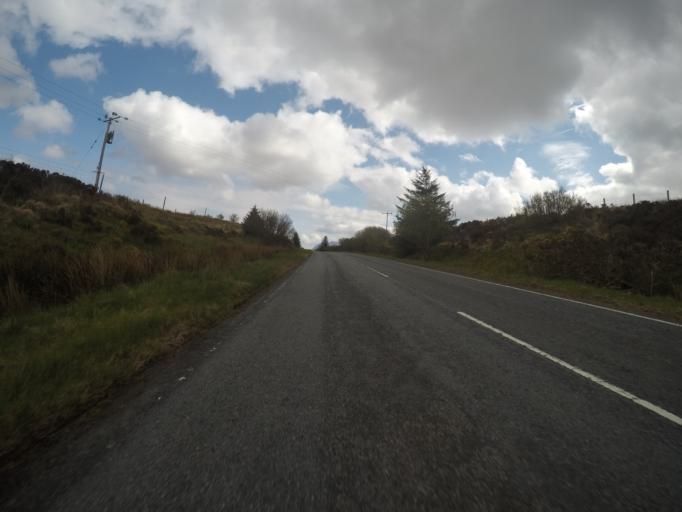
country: GB
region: Scotland
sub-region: Highland
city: Isle of Skye
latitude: 57.3338
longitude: -6.3491
